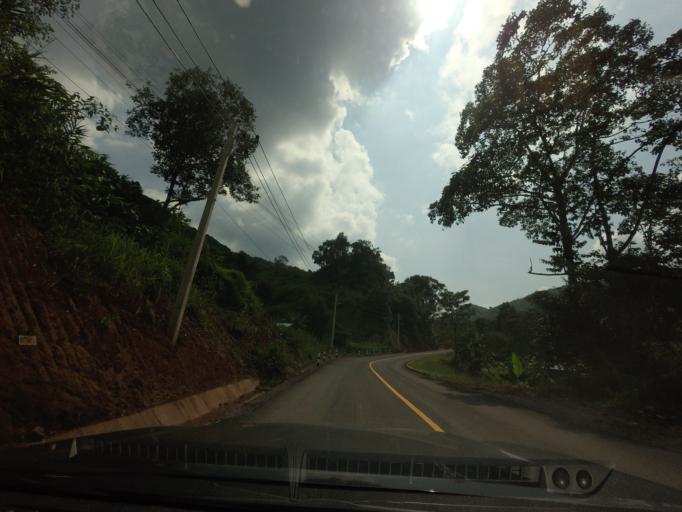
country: TH
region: Nan
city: Bo Kluea
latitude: 19.1950
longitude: 101.1825
